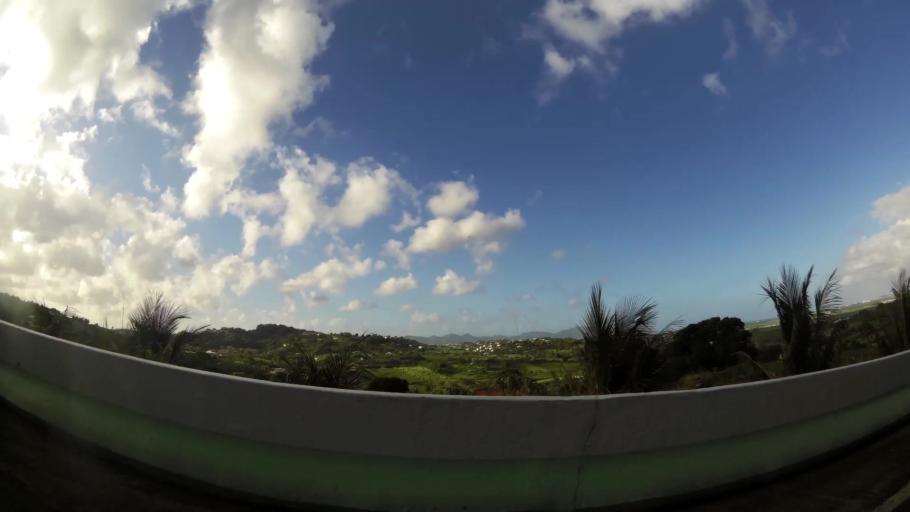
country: MQ
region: Martinique
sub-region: Martinique
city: Ducos
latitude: 14.6014
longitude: -60.9569
